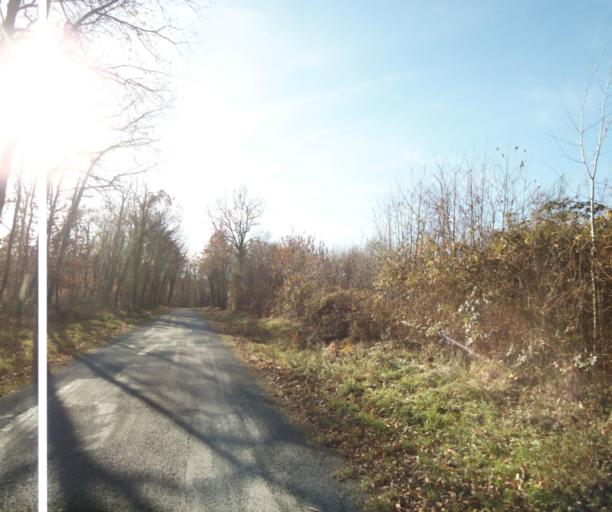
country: FR
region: Poitou-Charentes
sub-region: Departement de la Charente-Maritime
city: Ecoyeux
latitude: 45.7649
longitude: -0.5061
